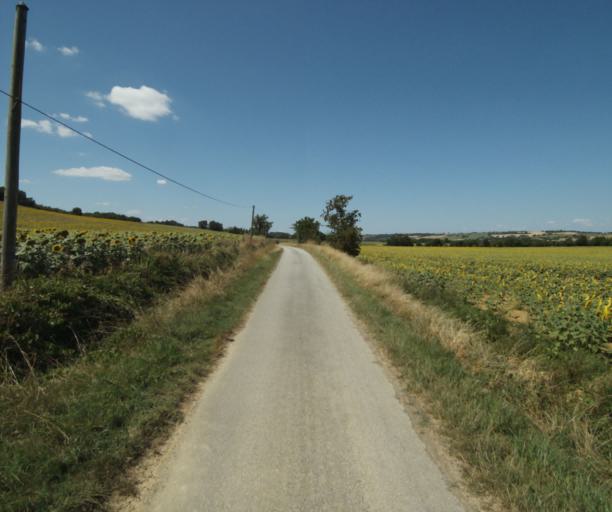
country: FR
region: Midi-Pyrenees
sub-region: Departement de la Haute-Garonne
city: Saint-Felix-Lauragais
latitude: 43.4673
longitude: 1.8874
